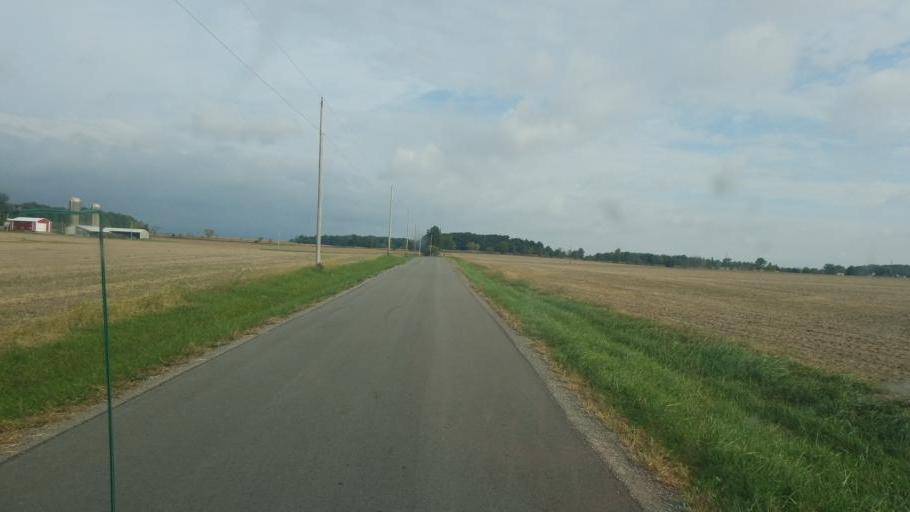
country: US
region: Ohio
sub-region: Wyandot County
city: Carey
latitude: 41.0296
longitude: -83.4484
